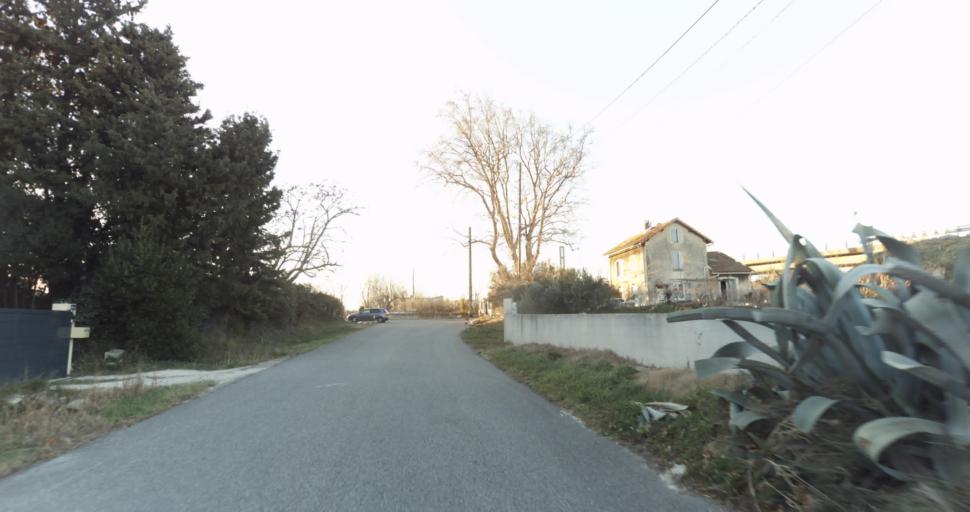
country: FR
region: Provence-Alpes-Cote d'Azur
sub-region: Departement des Bouches-du-Rhone
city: Rognonas
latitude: 43.8962
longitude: 4.7837
